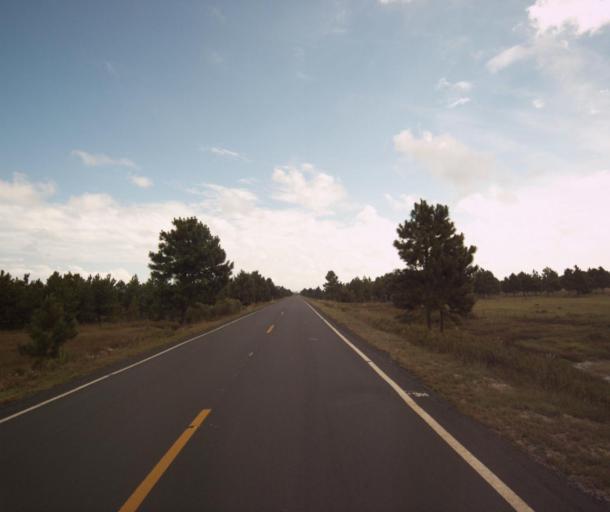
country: BR
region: Rio Grande do Sul
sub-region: Tapes
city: Tapes
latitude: -31.4317
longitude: -51.1901
